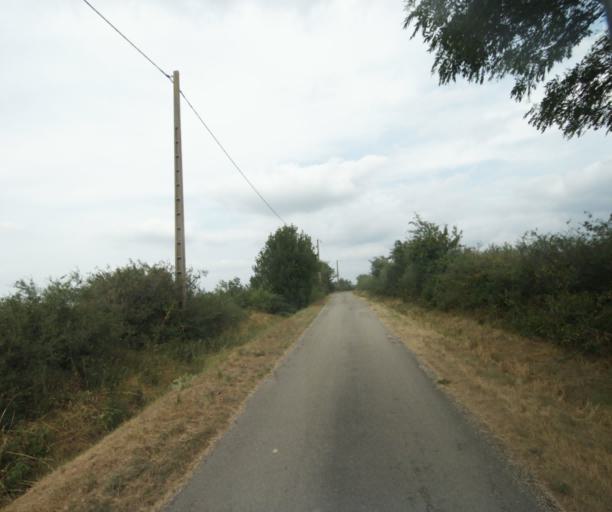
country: FR
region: Midi-Pyrenees
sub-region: Departement de la Haute-Garonne
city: Revel
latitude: 43.4427
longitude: 2.0037
